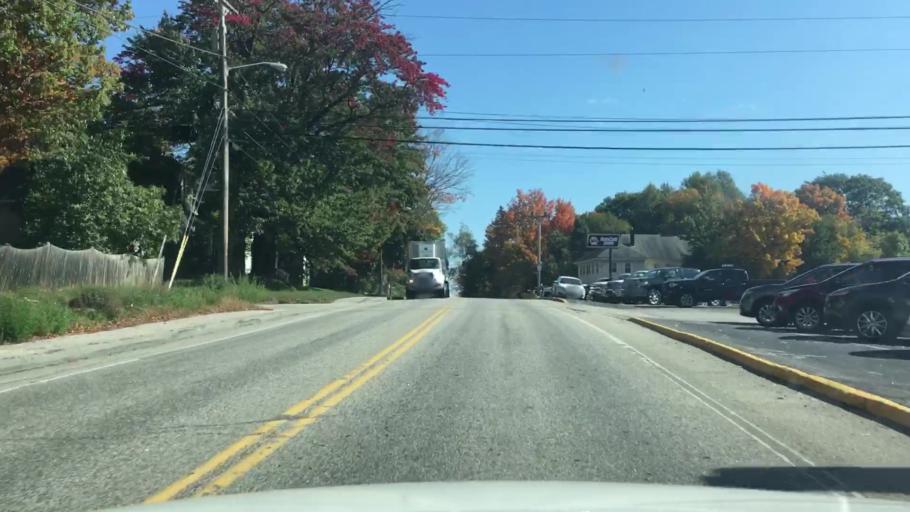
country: US
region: Maine
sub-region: Androscoggin County
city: Lisbon Falls
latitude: 43.9947
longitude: -70.0577
